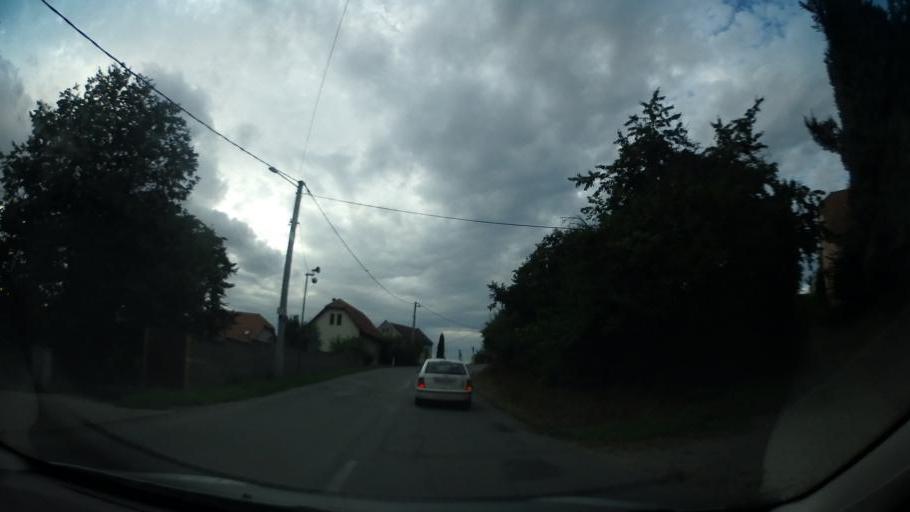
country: CZ
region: South Moravian
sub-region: Okres Blansko
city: Boskovice
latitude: 49.5407
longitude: 16.7037
